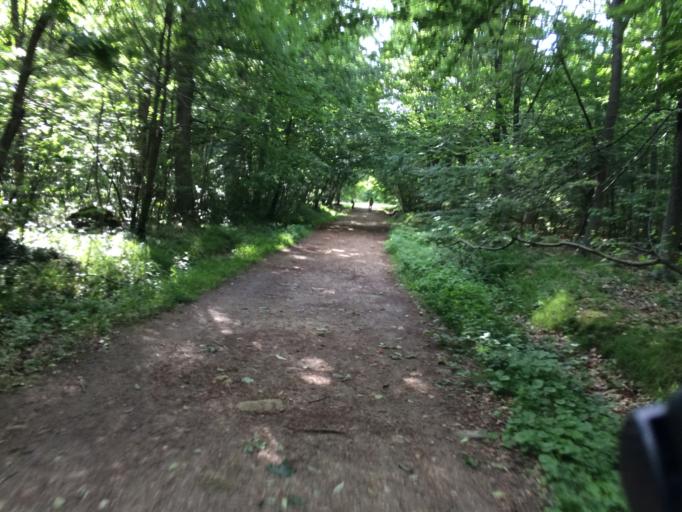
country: FR
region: Ile-de-France
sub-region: Departement de l'Essonne
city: Igny
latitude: 48.7514
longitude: 2.2426
